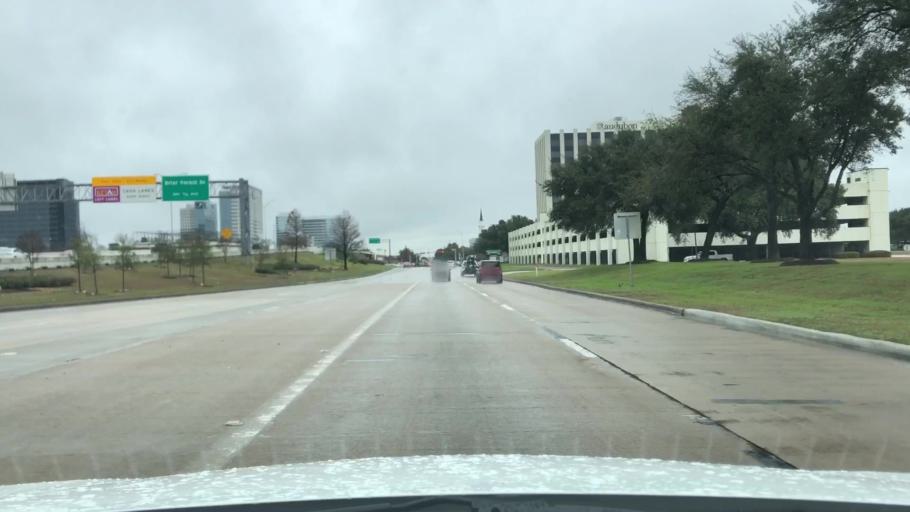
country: US
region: Texas
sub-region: Harris County
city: Bunker Hill Village
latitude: 29.7338
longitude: -95.5570
